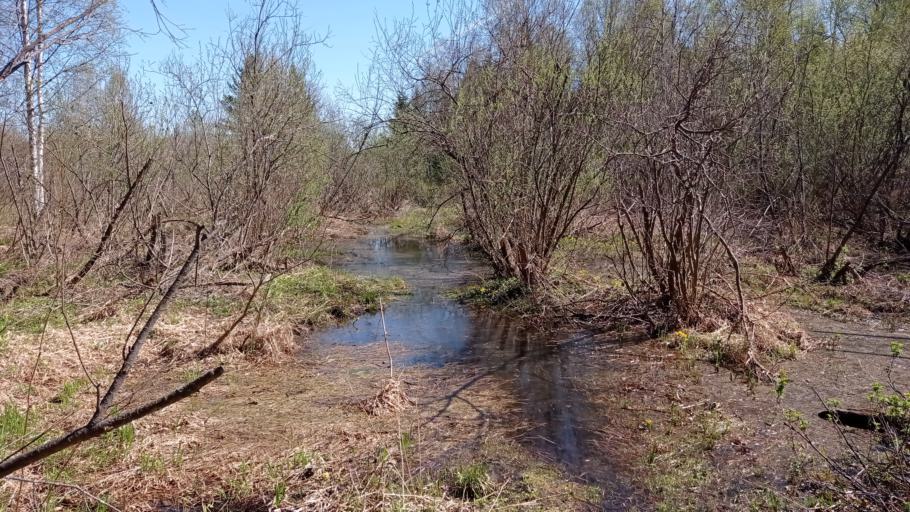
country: RU
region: Tomsk
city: Timiryazevskoye
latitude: 56.3868
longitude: 84.7519
